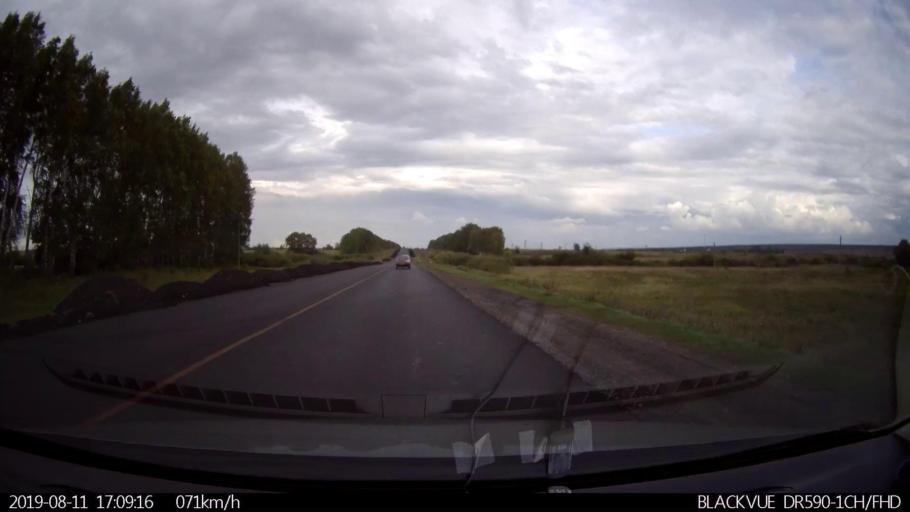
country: RU
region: Ulyanovsk
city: Mayna
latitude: 54.2954
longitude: 47.8527
